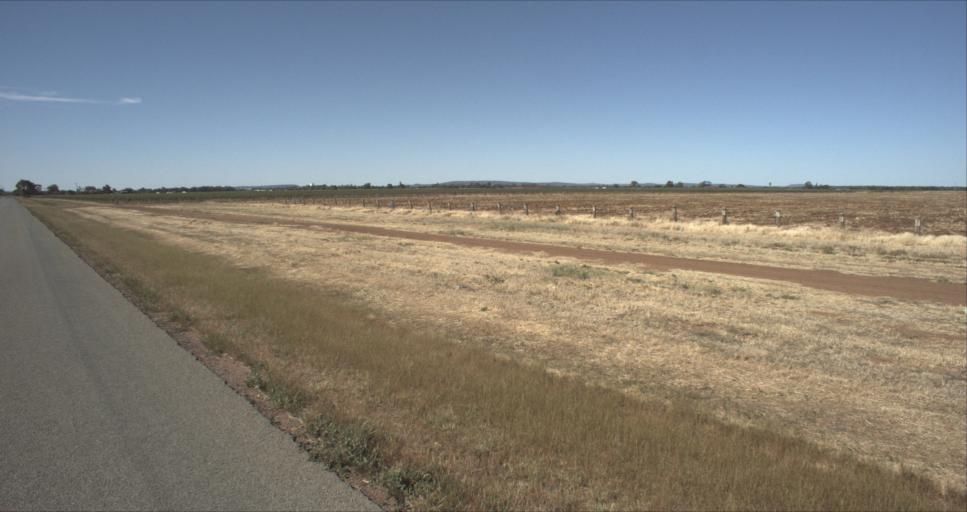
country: AU
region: New South Wales
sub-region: Leeton
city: Leeton
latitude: -34.5826
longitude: 146.3795
